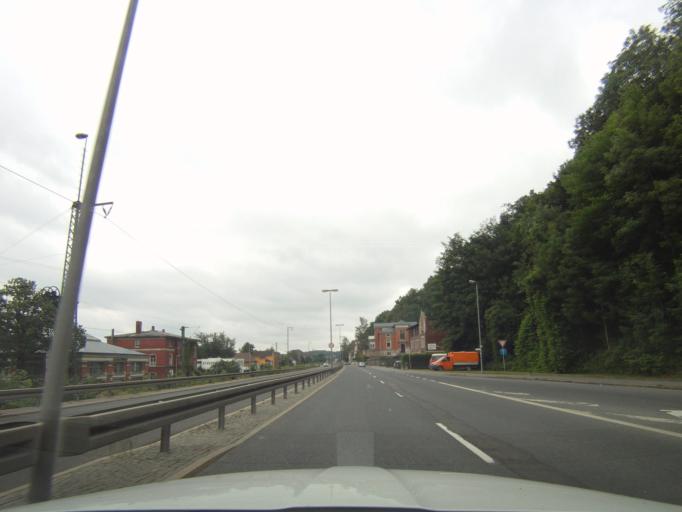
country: DE
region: Bavaria
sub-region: Upper Franconia
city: Coburg
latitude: 50.2591
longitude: 10.9575
